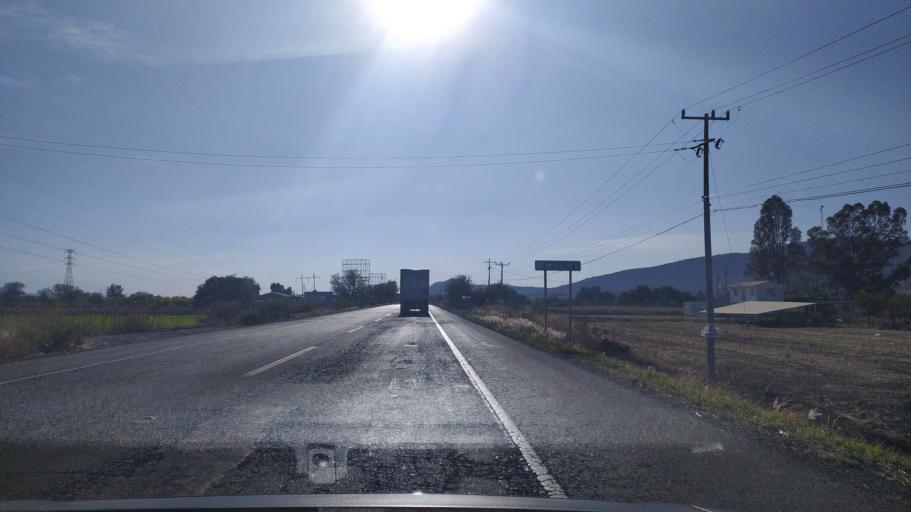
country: MX
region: Jalisco
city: Jamay
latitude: 20.2937
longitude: -102.6529
